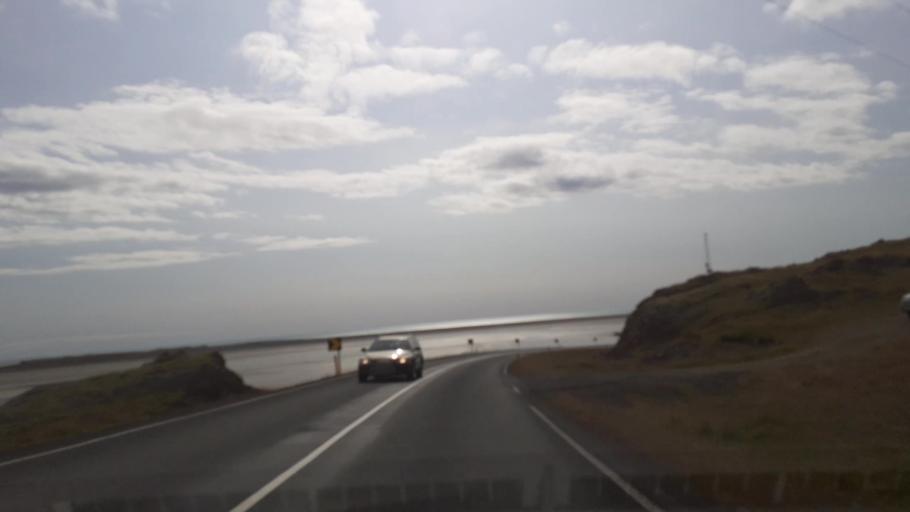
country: IS
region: East
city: Hoefn
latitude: 64.1934
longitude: -15.7447
